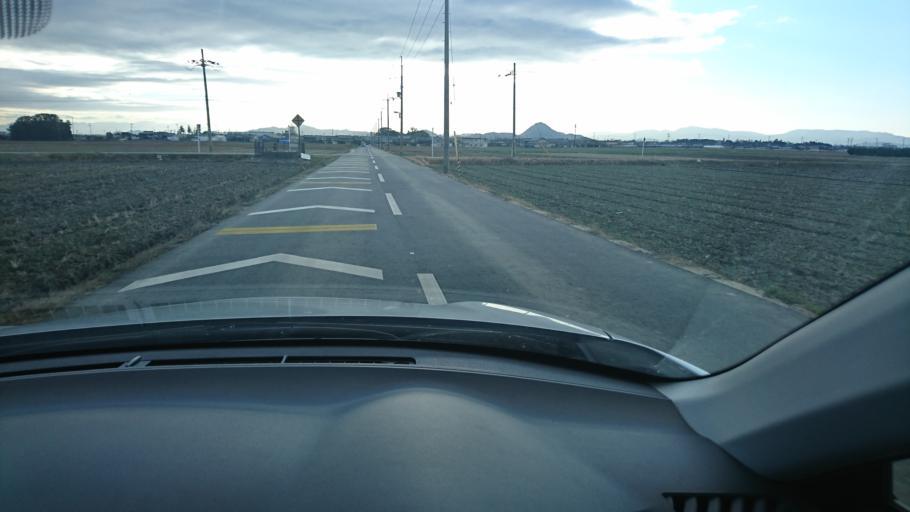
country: JP
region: Shiga Prefecture
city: Moriyama
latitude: 35.1131
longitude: 135.9764
